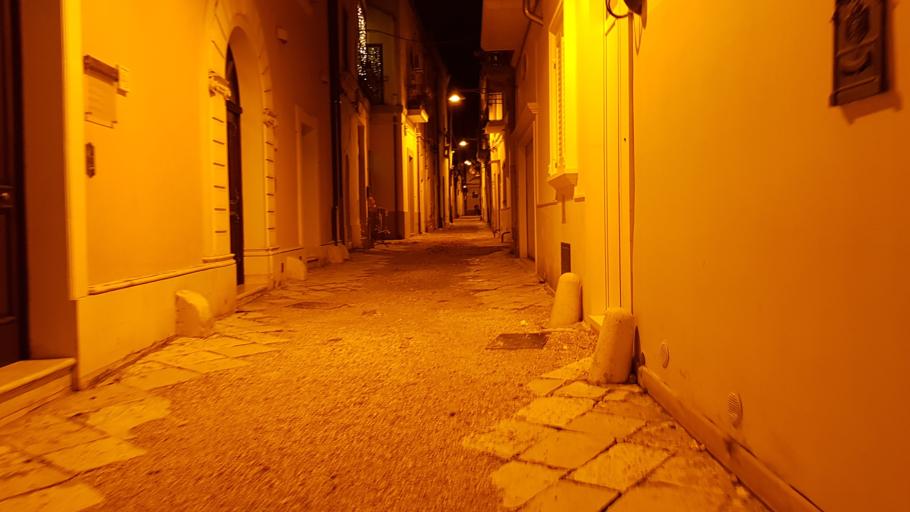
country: IT
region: Apulia
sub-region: Provincia di Brindisi
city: Brindisi
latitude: 40.6383
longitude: 17.9426
